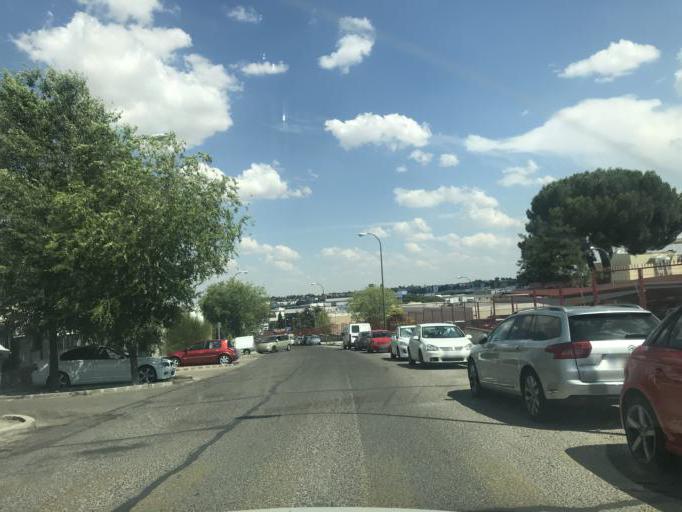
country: ES
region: Madrid
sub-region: Provincia de Madrid
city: Alcobendas
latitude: 40.5368
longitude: -3.6535
